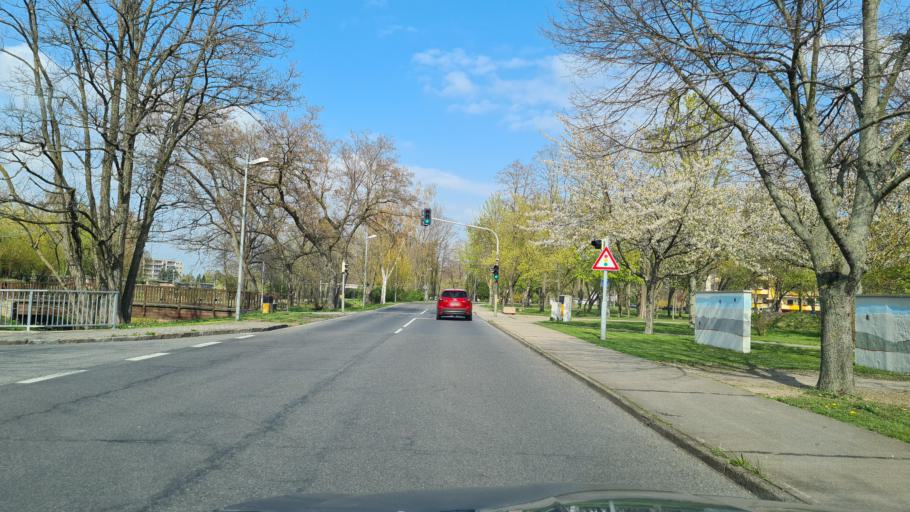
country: DE
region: Saxony
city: Nauwalde
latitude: 51.4127
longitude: 13.4543
